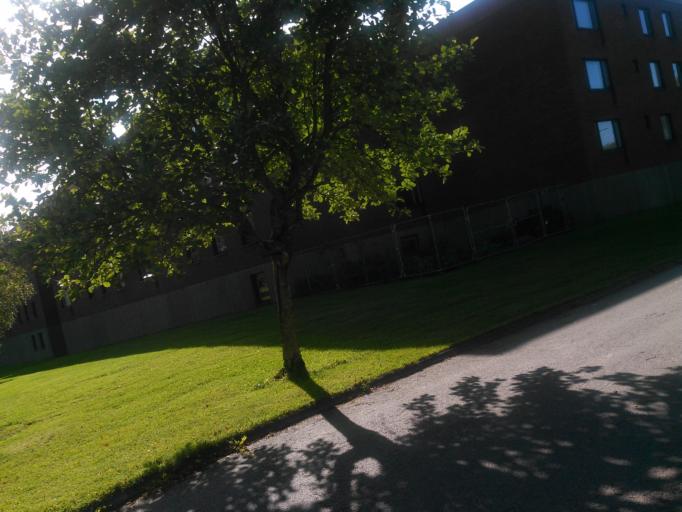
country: SE
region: Vaesterbotten
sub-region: Umea Kommun
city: Umea
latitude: 63.8132
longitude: 20.3220
